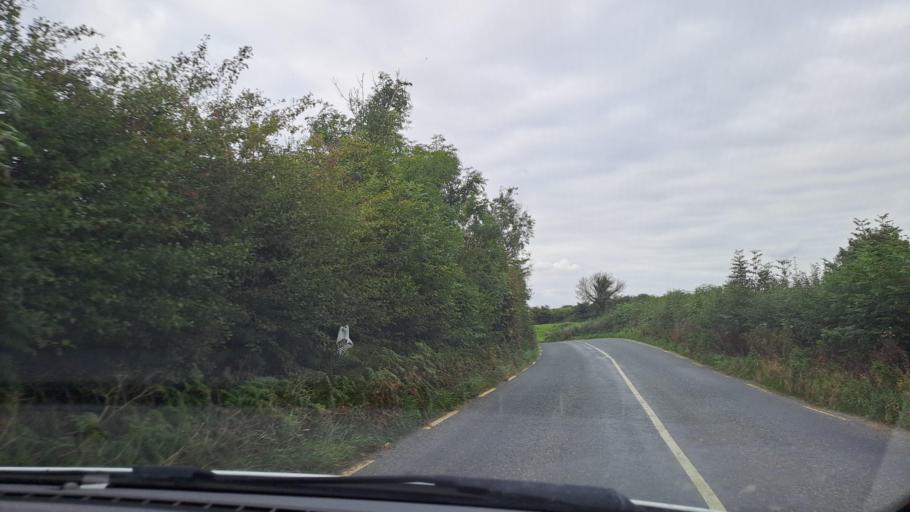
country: IE
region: Ulster
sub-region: An Cabhan
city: Bailieborough
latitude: 53.9843
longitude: -6.8834
